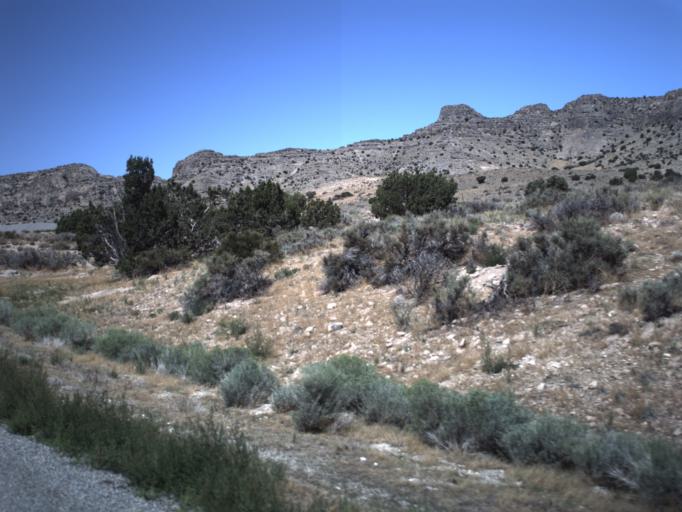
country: US
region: Utah
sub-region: Beaver County
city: Milford
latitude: 39.0746
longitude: -113.6368
